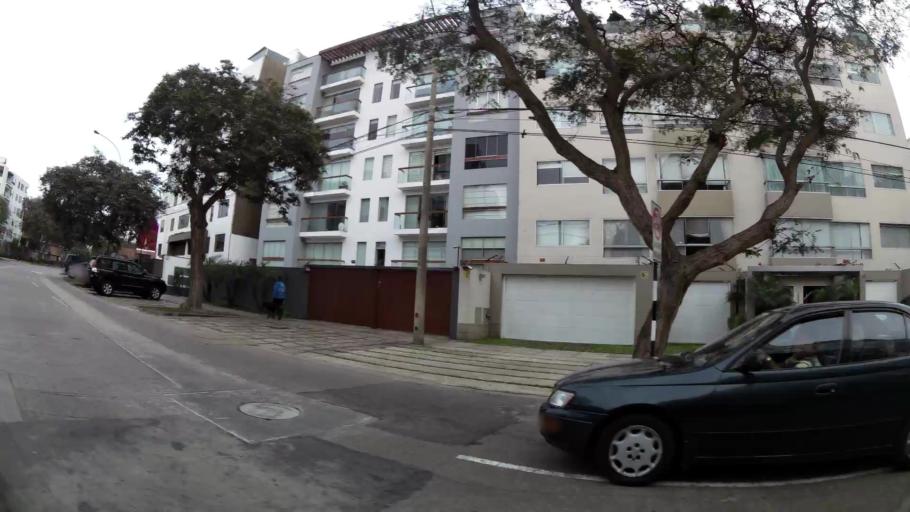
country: PE
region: Lima
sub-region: Lima
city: San Isidro
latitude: -12.1104
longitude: -77.0445
